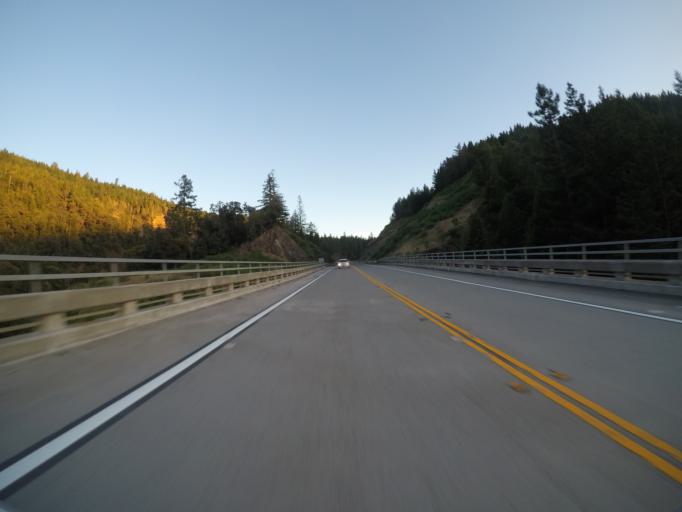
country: US
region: California
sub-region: Humboldt County
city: Redway
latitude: 39.9268
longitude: -123.7609
